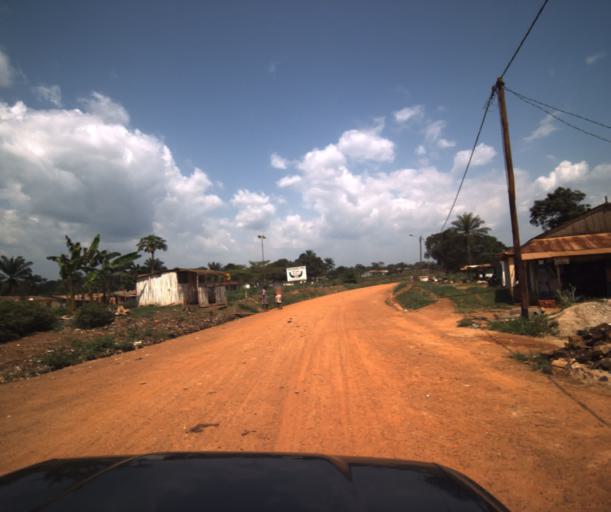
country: CM
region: Centre
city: Eseka
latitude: 3.5472
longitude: 11.0341
